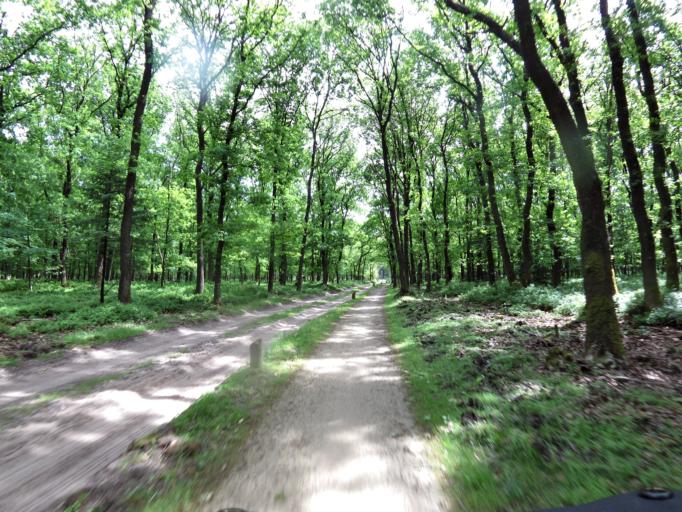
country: NL
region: Gelderland
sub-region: Gemeente Apeldoorn
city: Uddel
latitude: 52.2993
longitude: 5.8213
